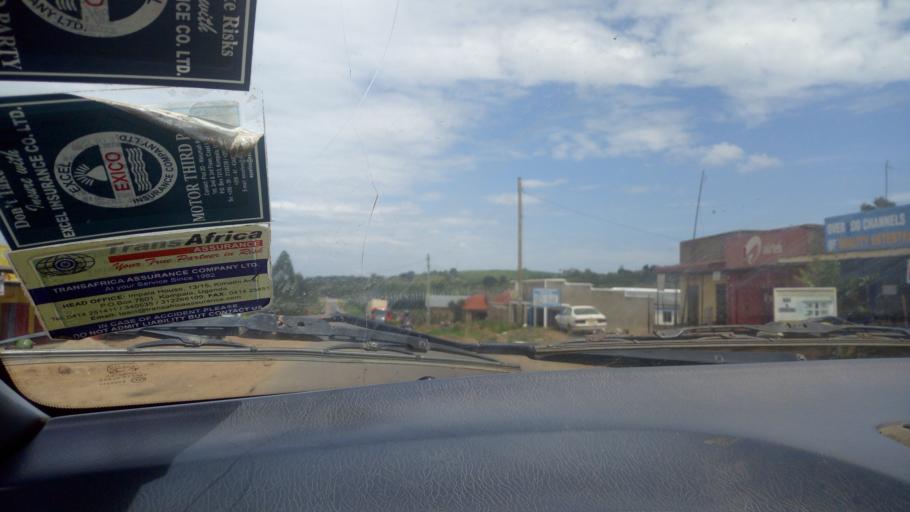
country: UG
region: Western Region
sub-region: Mbarara District
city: Bwizibwera
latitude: -0.4071
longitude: 30.5682
